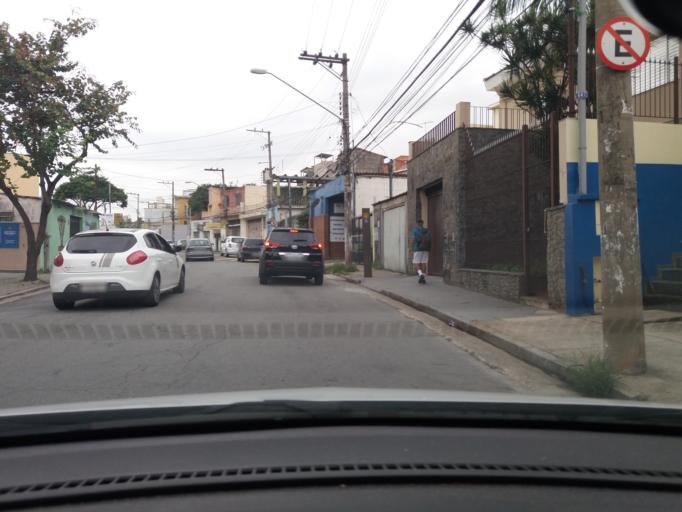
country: BR
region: Sao Paulo
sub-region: Sao Paulo
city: Sao Paulo
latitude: -23.4811
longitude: -46.6274
